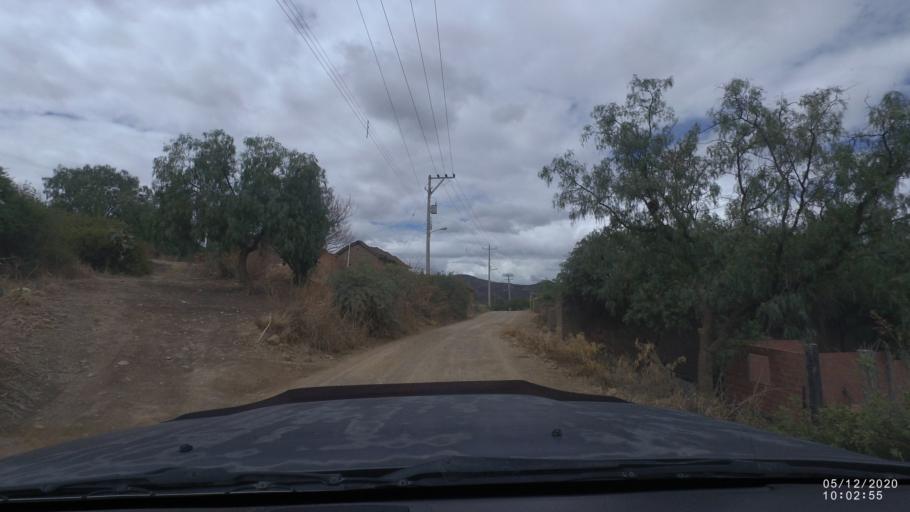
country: BO
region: Cochabamba
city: Sipe Sipe
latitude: -17.4539
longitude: -66.2860
